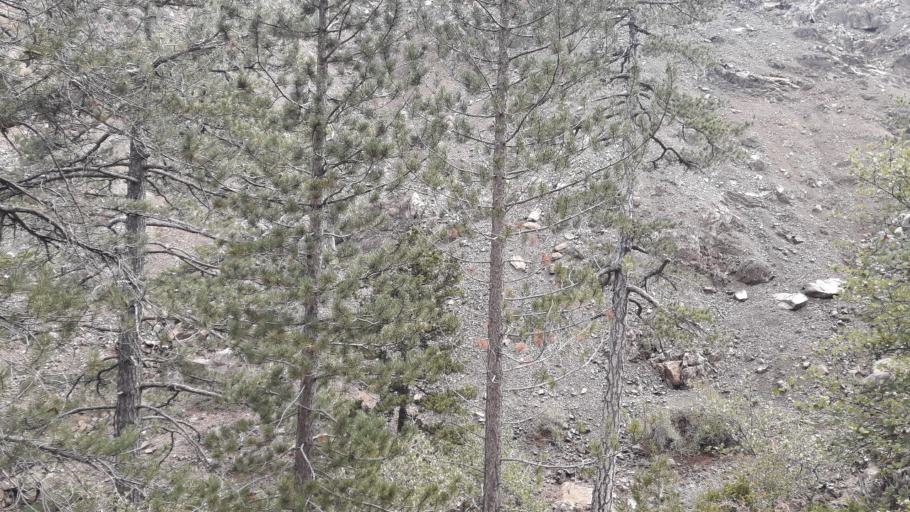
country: CY
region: Lefkosia
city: Kakopetria
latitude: 34.9418
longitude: 32.8802
